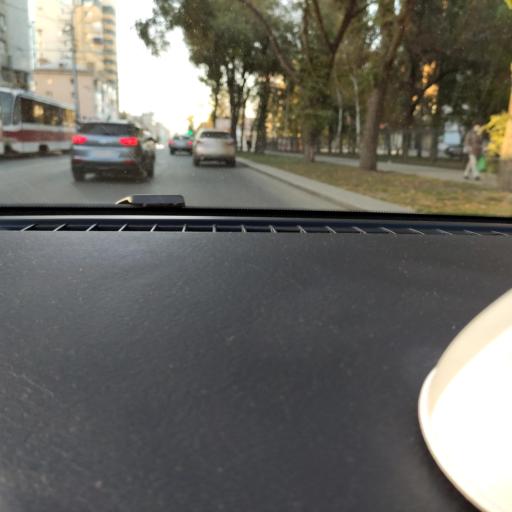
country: RU
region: Samara
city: Samara
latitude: 53.2016
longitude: 50.1283
